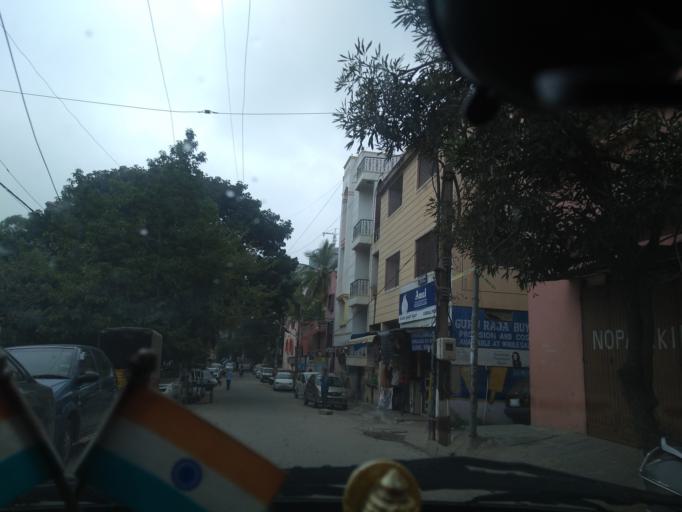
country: IN
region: Karnataka
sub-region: Bangalore Urban
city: Bangalore
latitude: 13.0091
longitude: 77.5588
